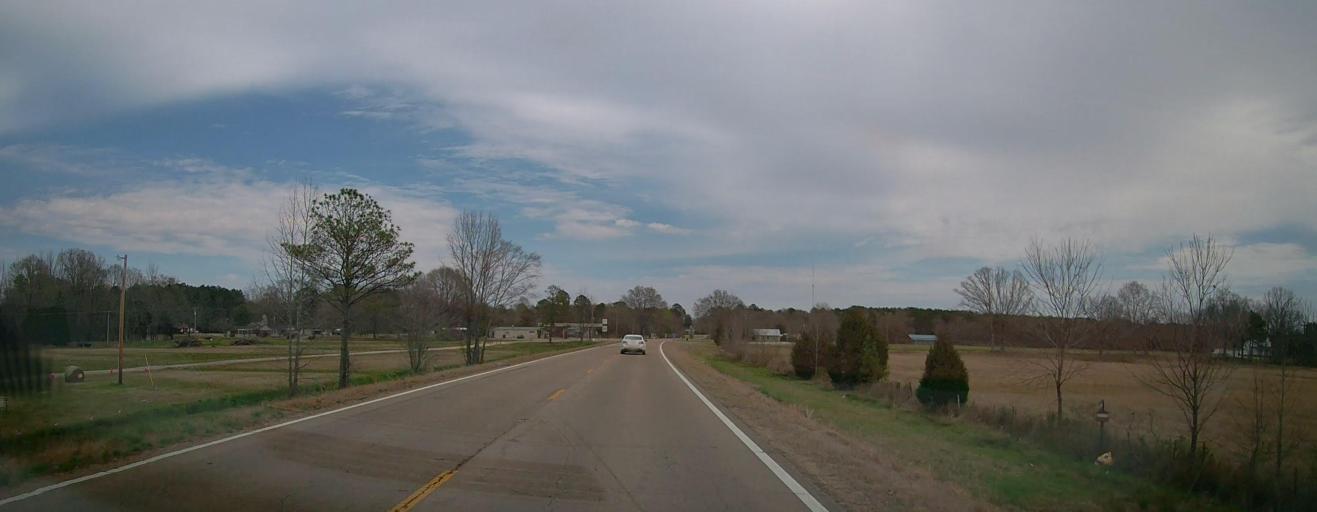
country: US
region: Mississippi
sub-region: Itawamba County
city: Mantachie
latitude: 34.2669
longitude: -88.5609
